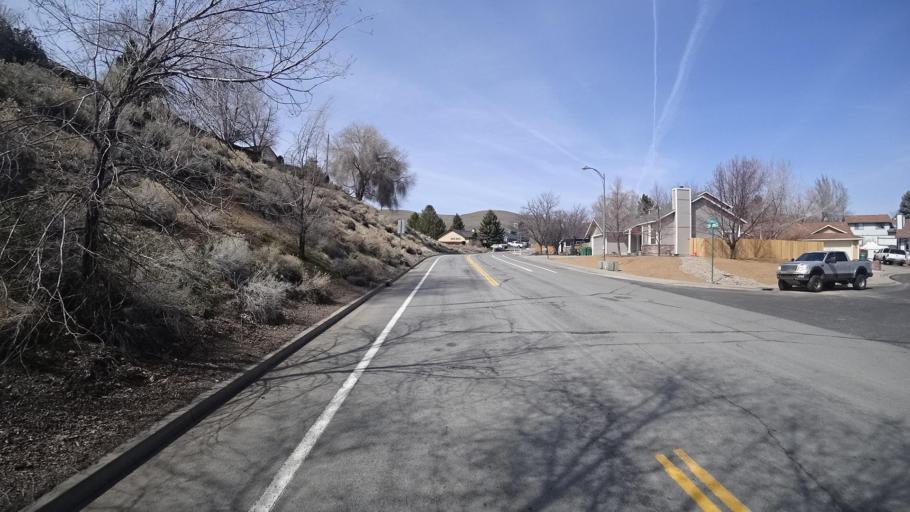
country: US
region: Nevada
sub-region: Washoe County
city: Reno
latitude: 39.5470
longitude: -119.8441
